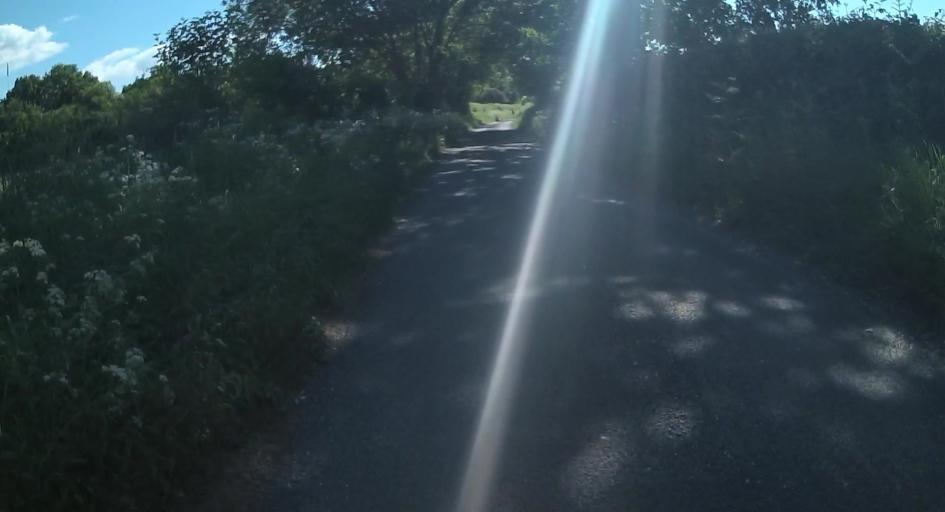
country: GB
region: England
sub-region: Hampshire
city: Old Basing
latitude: 51.2475
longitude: -1.0289
